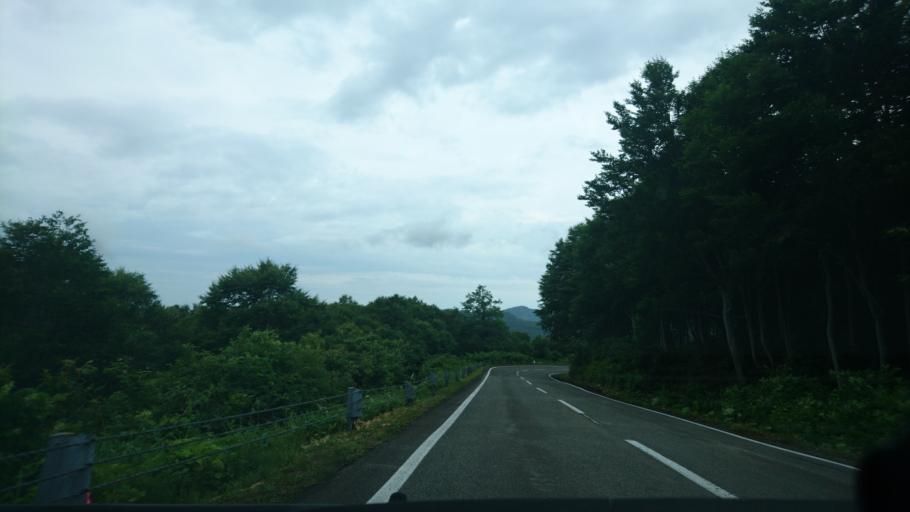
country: JP
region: Akita
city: Yuzawa
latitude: 39.1527
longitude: 140.7551
